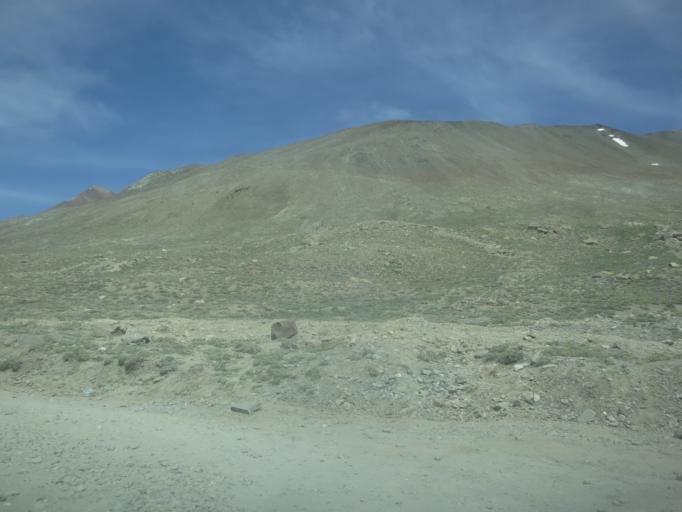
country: IN
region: Himachal Pradesh
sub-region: Kulu
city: Manali
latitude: 32.3946
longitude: 77.6350
